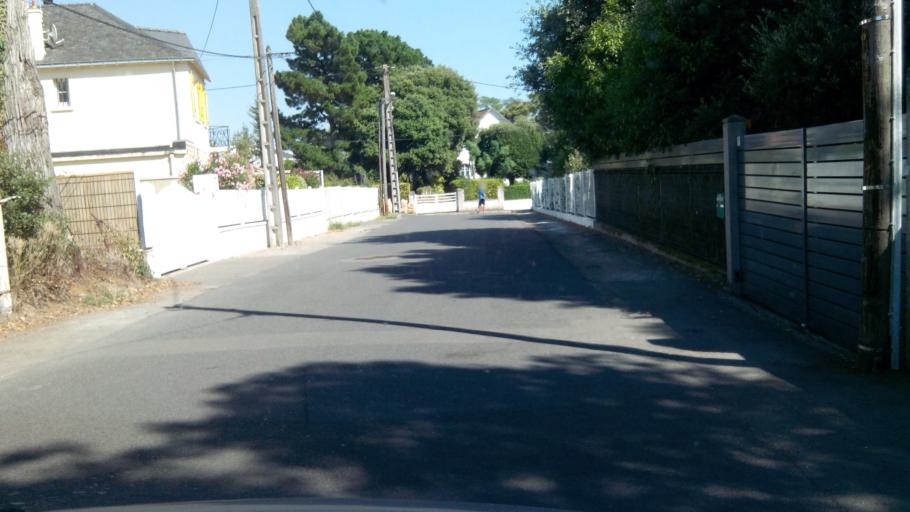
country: FR
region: Pays de la Loire
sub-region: Departement de la Loire-Atlantique
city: Pornichet
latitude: 47.2730
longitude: -2.3454
